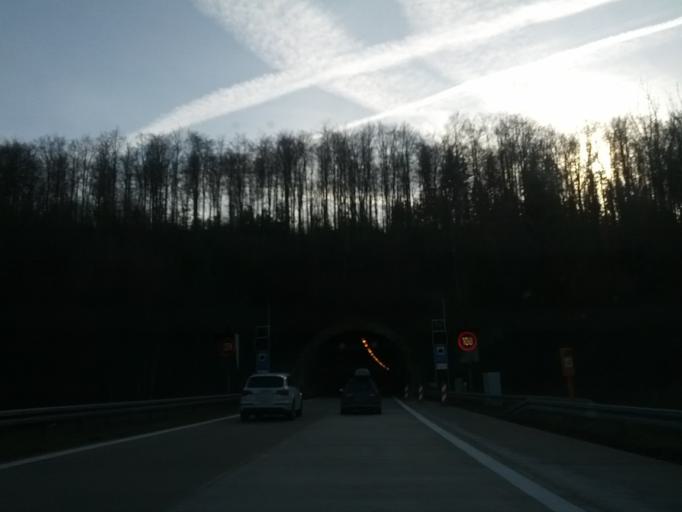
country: DE
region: Baden-Wuerttemberg
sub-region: Regierungsbezirk Stuttgart
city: Ellenberg
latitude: 49.0226
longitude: 10.1964
